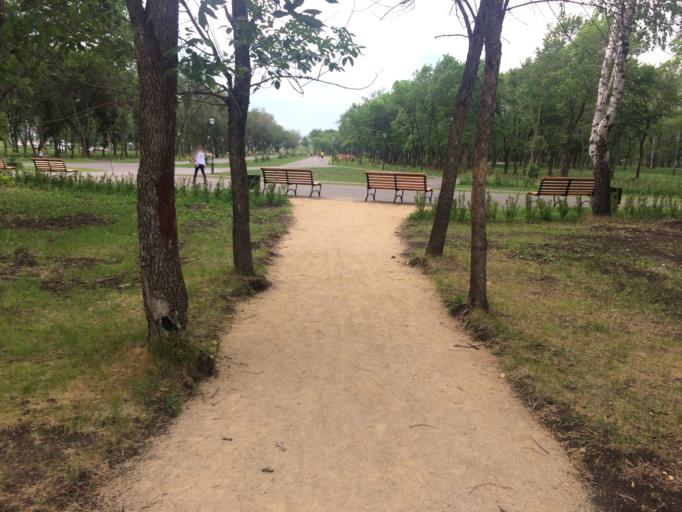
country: RU
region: Chelyabinsk
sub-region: Gorod Magnitogorsk
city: Magnitogorsk
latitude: 53.4017
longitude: 58.9929
